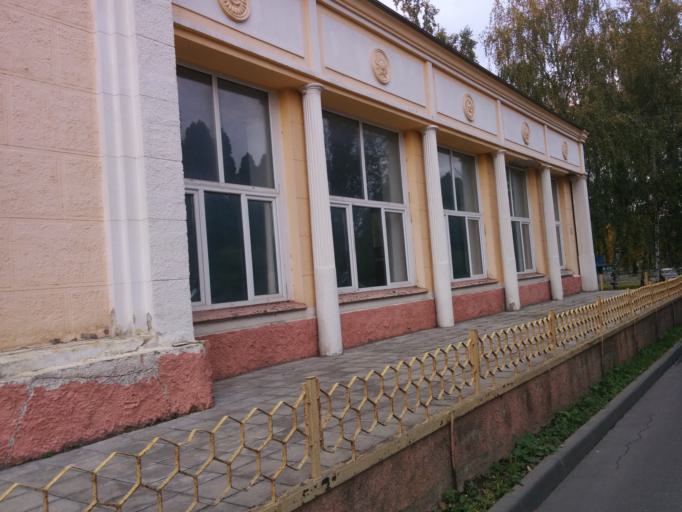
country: RU
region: Moscow
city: Ostankinskiy
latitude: 55.8364
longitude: 37.6165
